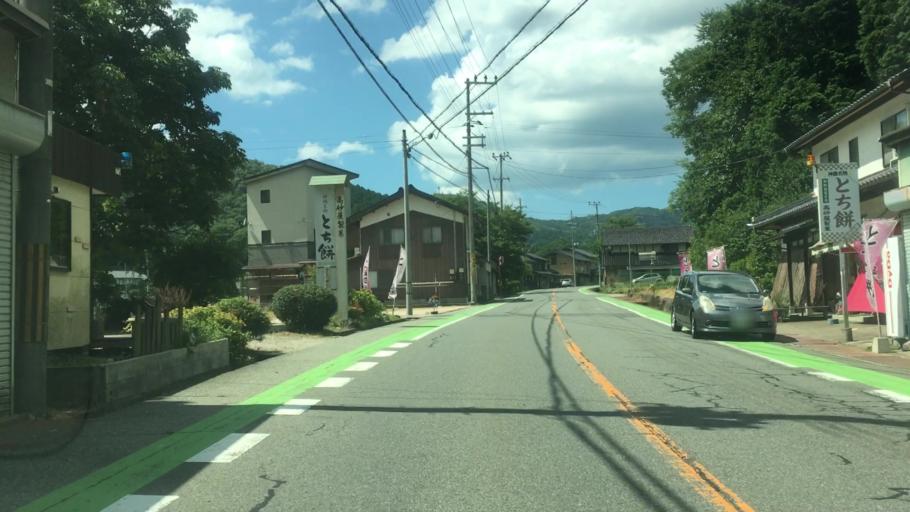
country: JP
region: Hyogo
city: Toyooka
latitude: 35.4773
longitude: 134.7095
